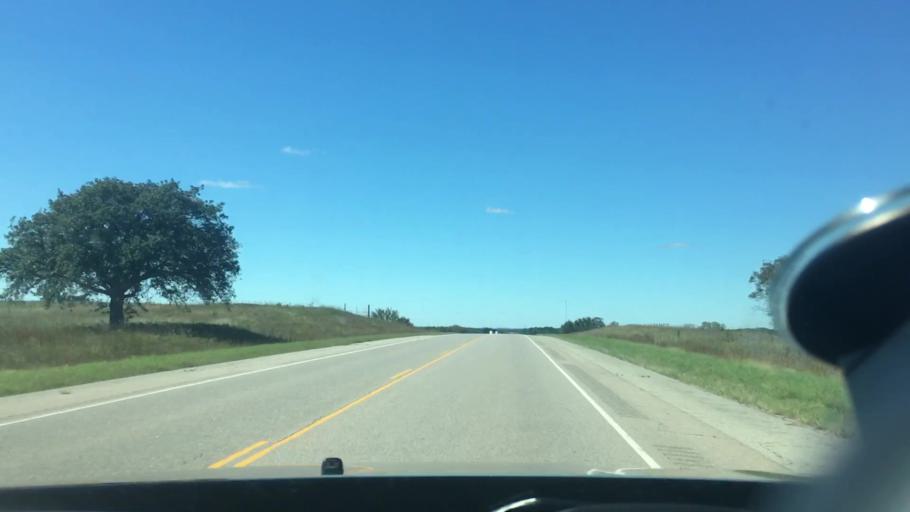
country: US
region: Oklahoma
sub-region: Coal County
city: Coalgate
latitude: 34.6183
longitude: -96.4496
